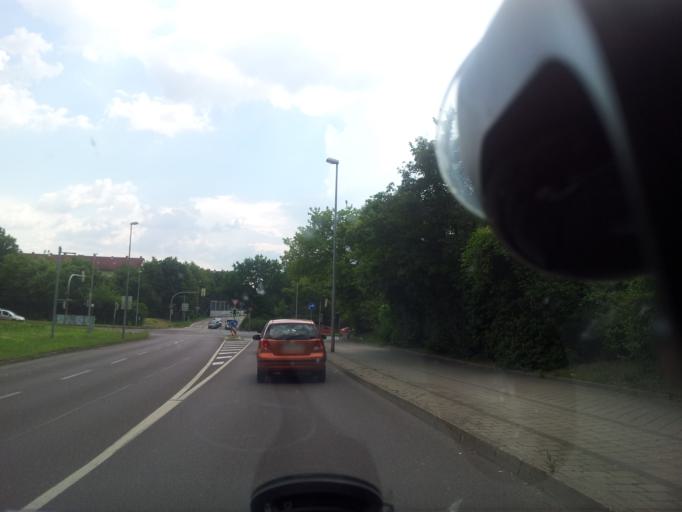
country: DE
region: Saxony-Anhalt
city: Magdeburg
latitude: 52.1120
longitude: 11.6116
